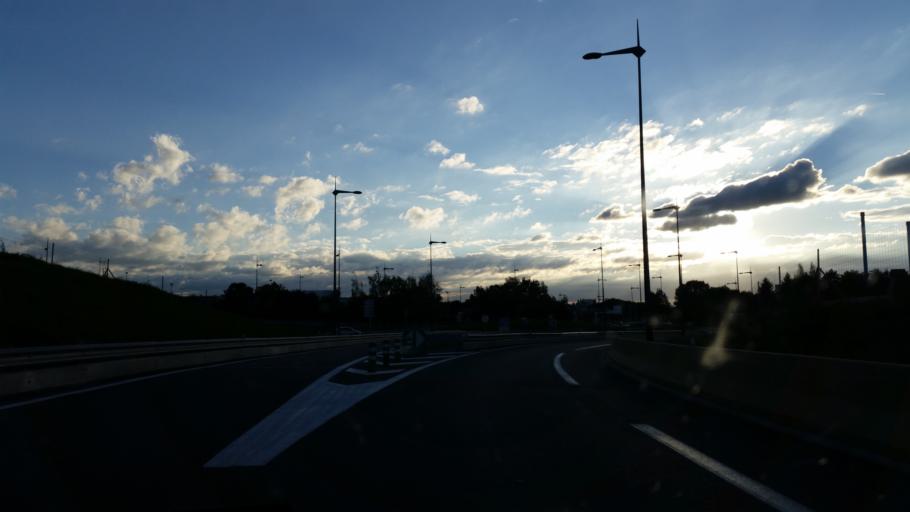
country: FR
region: Franche-Comte
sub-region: Departement du Doubs
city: Sochaux
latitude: 47.5018
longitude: 6.8203
